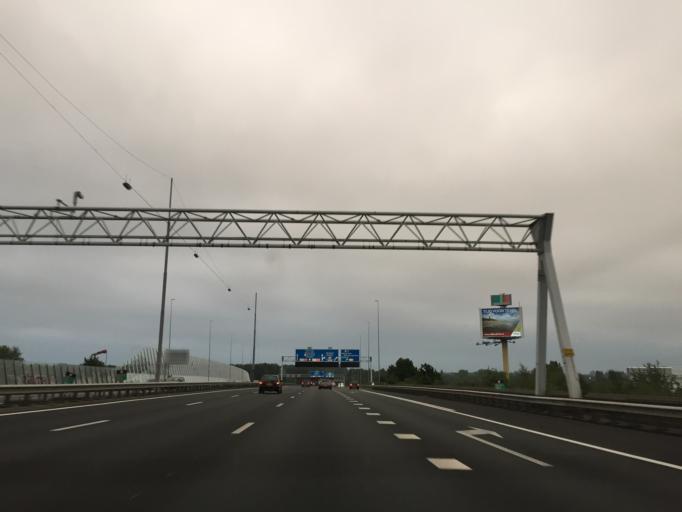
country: NL
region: North Holland
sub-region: Gemeente Diemen
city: Diemen
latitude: 52.3567
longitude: 4.9661
